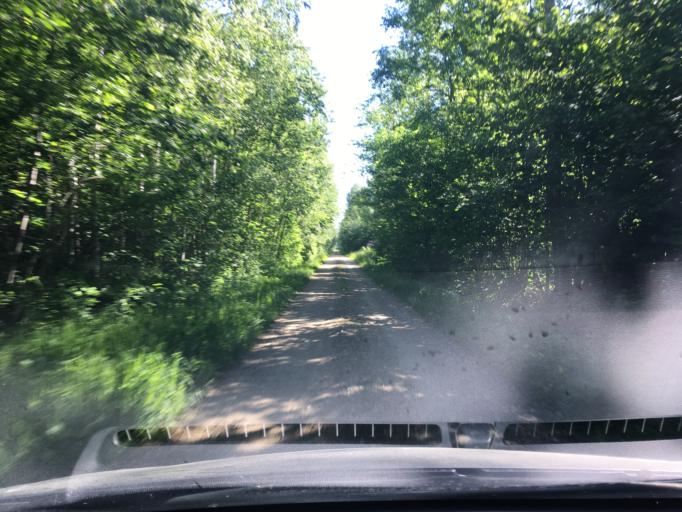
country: EE
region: Laeaene
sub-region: Lihula vald
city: Lihula
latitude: 58.6202
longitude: 23.7009
